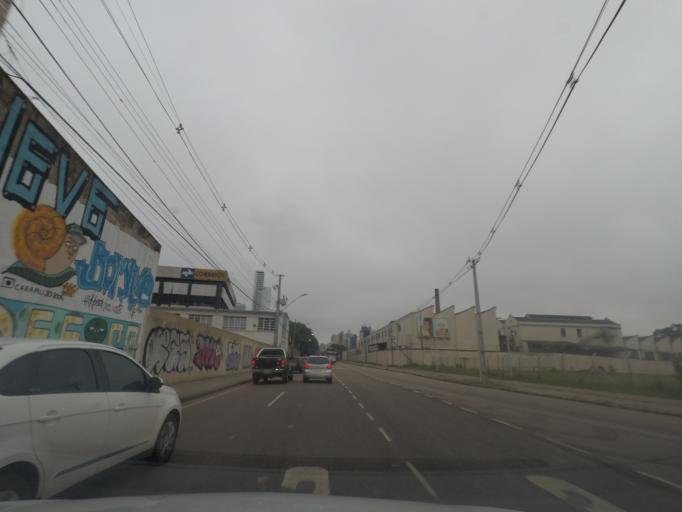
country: BR
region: Parana
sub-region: Curitiba
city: Curitiba
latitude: -25.4404
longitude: -49.2603
